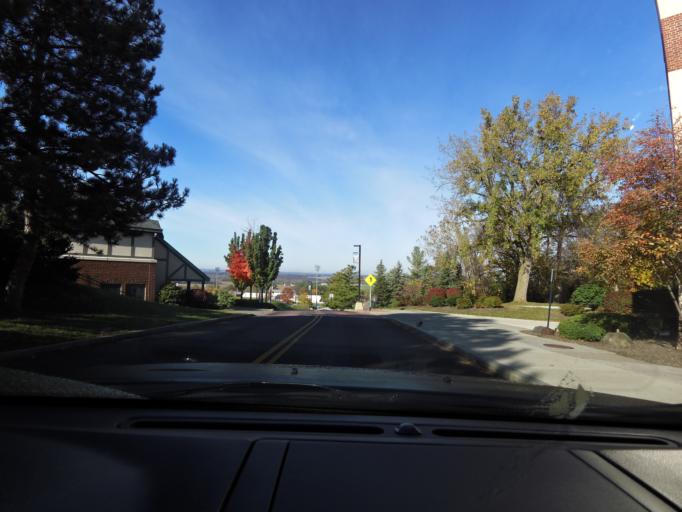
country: US
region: New York
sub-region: Livingston County
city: Geneseo
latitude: 42.7950
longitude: -77.8212
